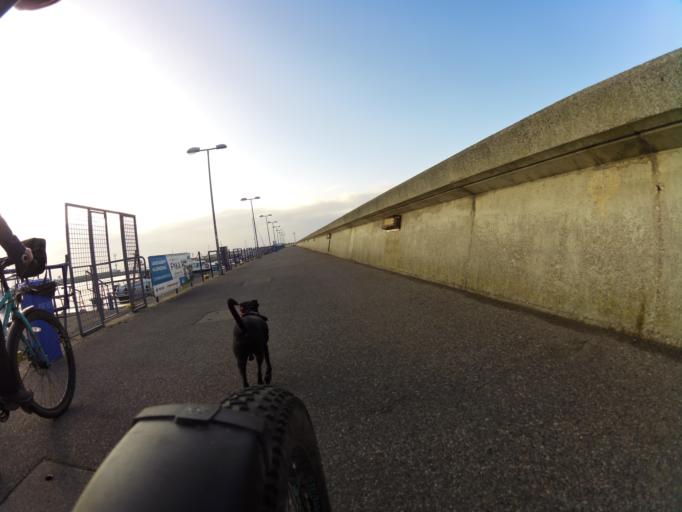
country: PL
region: Pomeranian Voivodeship
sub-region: Powiat pucki
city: Hel
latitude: 54.6028
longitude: 18.8000
